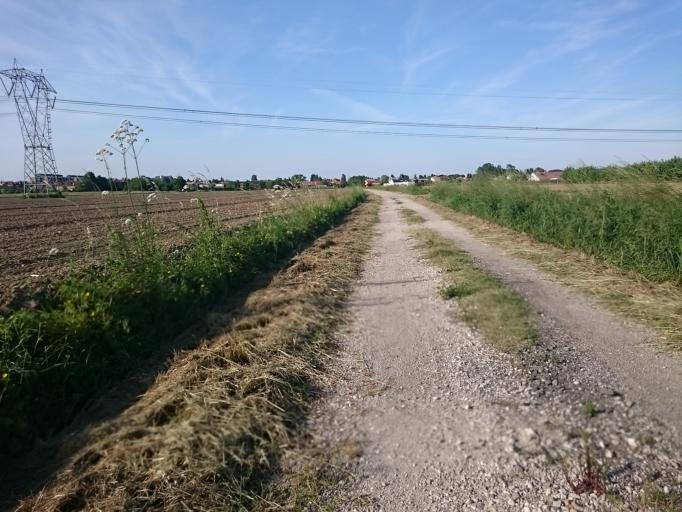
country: IT
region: Veneto
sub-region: Provincia di Padova
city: Mandriola-Sant'Agostino
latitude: 45.3624
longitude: 11.8302
